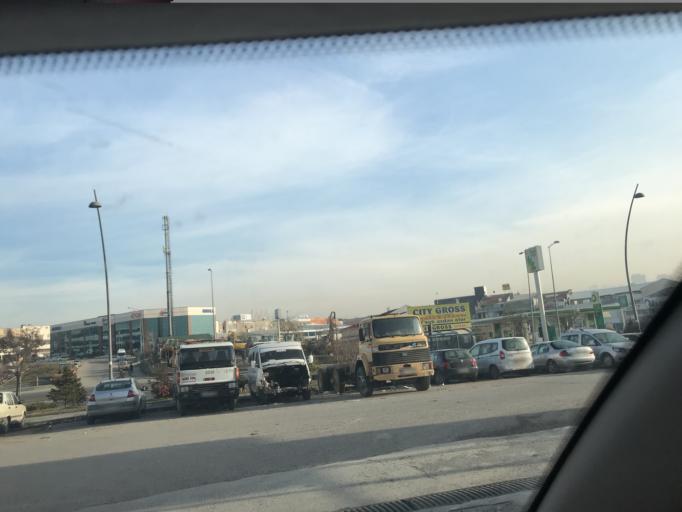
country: TR
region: Ankara
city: Batikent
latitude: 39.9635
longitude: 32.7539
